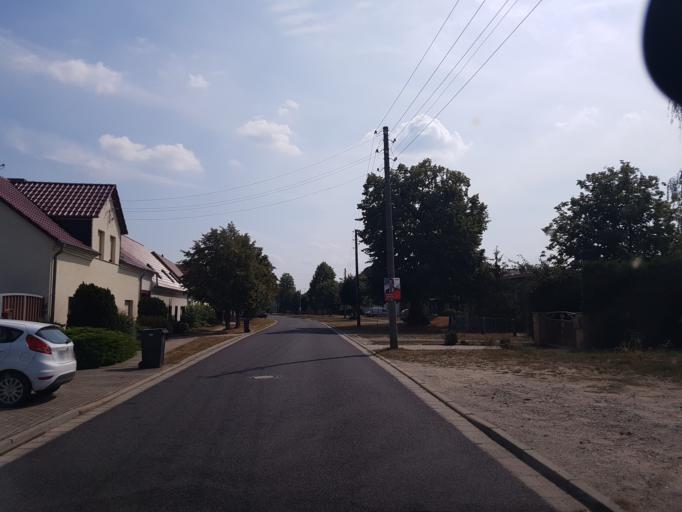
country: DE
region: Brandenburg
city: Finsterwalde
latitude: 51.6665
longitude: 13.7314
